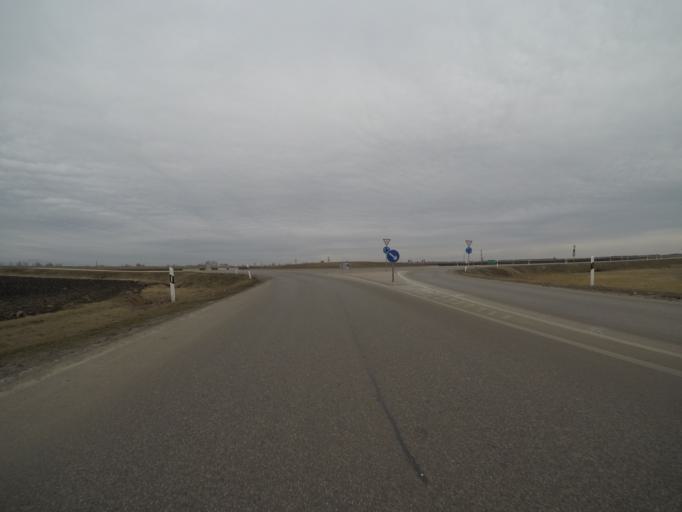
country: HU
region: Jasz-Nagykun-Szolnok
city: Jaszbereny
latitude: 47.5120
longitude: 19.9443
